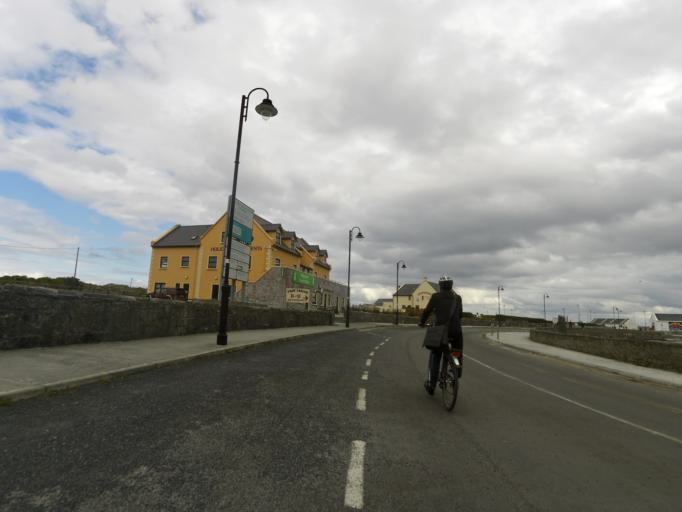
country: IE
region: Connaught
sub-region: County Galway
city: Oughterard
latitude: 53.1199
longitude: -9.6674
